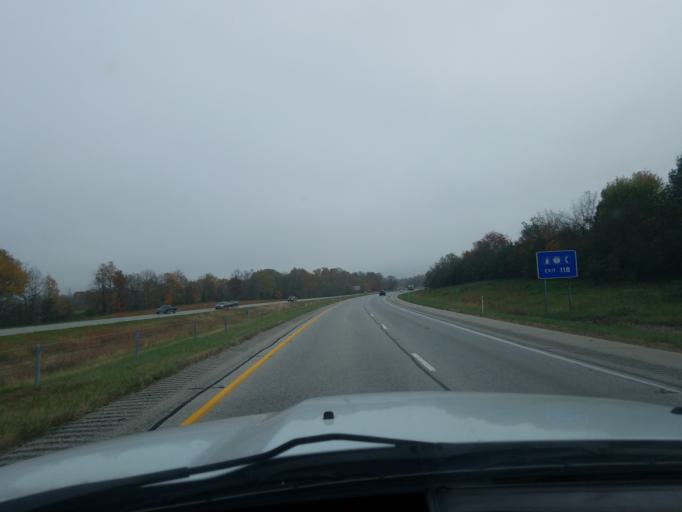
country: US
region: Indiana
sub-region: Floyd County
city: Georgetown
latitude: 38.2840
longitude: -85.9339
